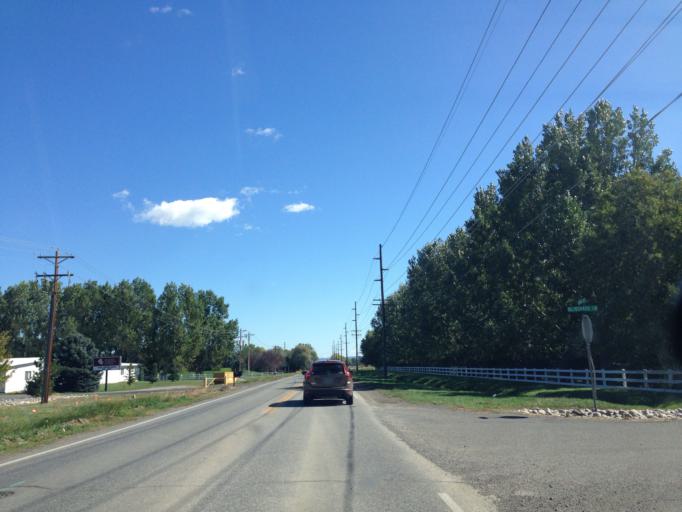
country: US
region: Montana
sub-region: Yellowstone County
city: Billings
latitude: 45.7840
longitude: -108.6312
